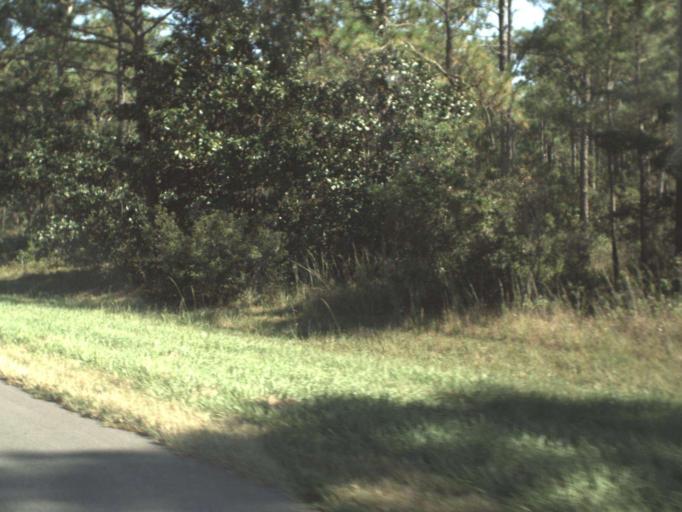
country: US
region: Florida
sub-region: Walton County
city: Miramar Beach
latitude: 30.4845
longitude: -86.2786
